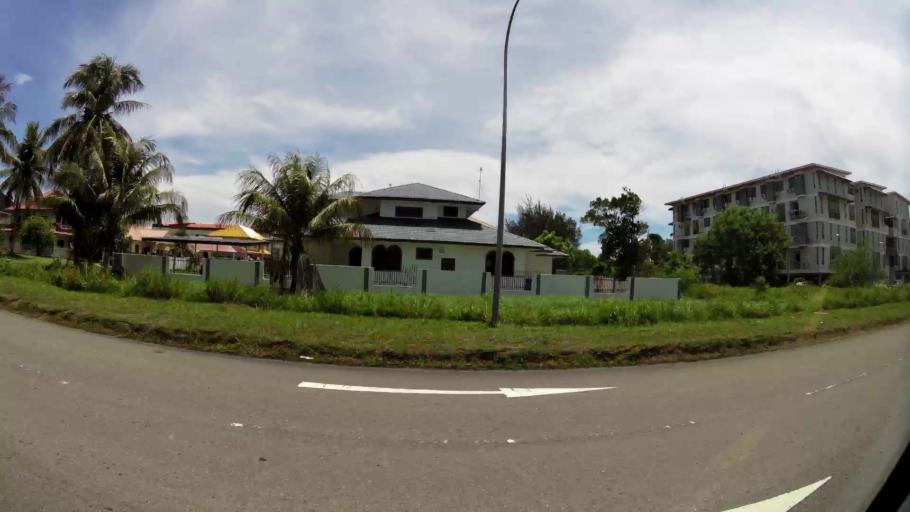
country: BN
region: Belait
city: Kuala Belait
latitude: 4.5908
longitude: 114.2308
